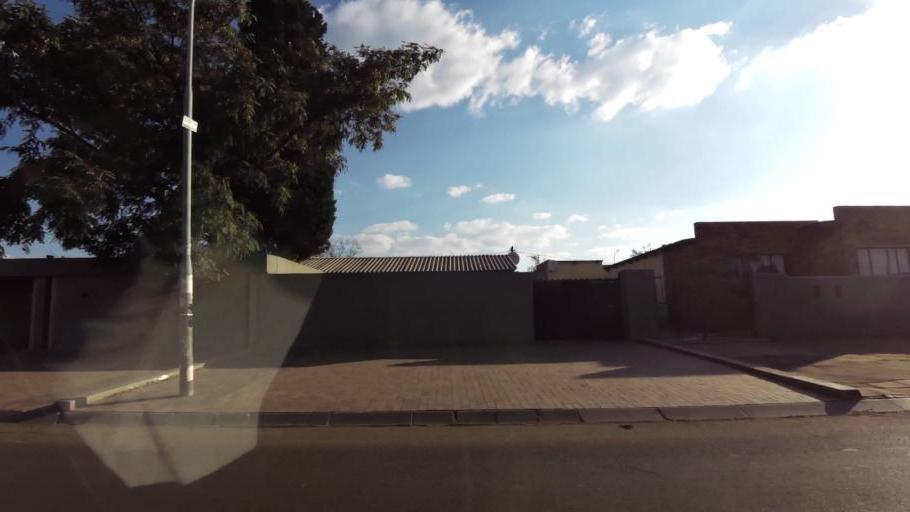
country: ZA
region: Gauteng
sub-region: City of Johannesburg Metropolitan Municipality
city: Soweto
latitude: -26.2317
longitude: 27.9011
